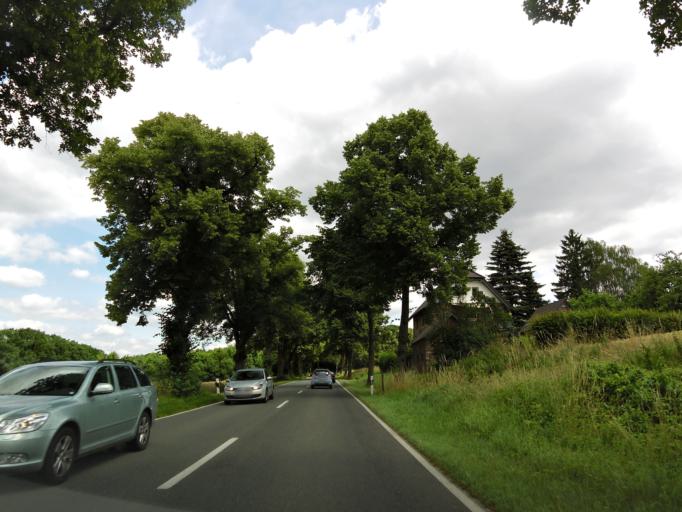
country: DE
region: North Rhine-Westphalia
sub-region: Regierungsbezirk Detmold
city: Hoexter
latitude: 51.7648
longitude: 9.4103
